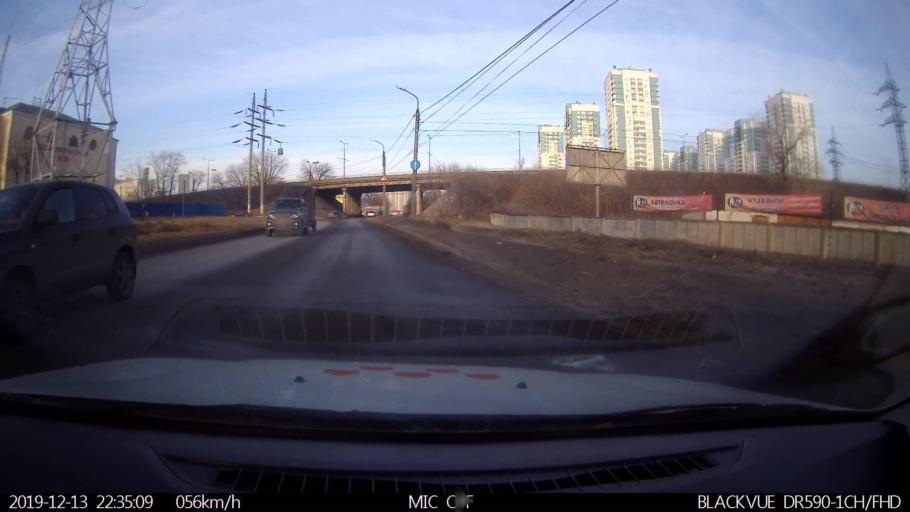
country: RU
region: Nizjnij Novgorod
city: Nizhniy Novgorod
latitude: 56.2978
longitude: 43.9506
